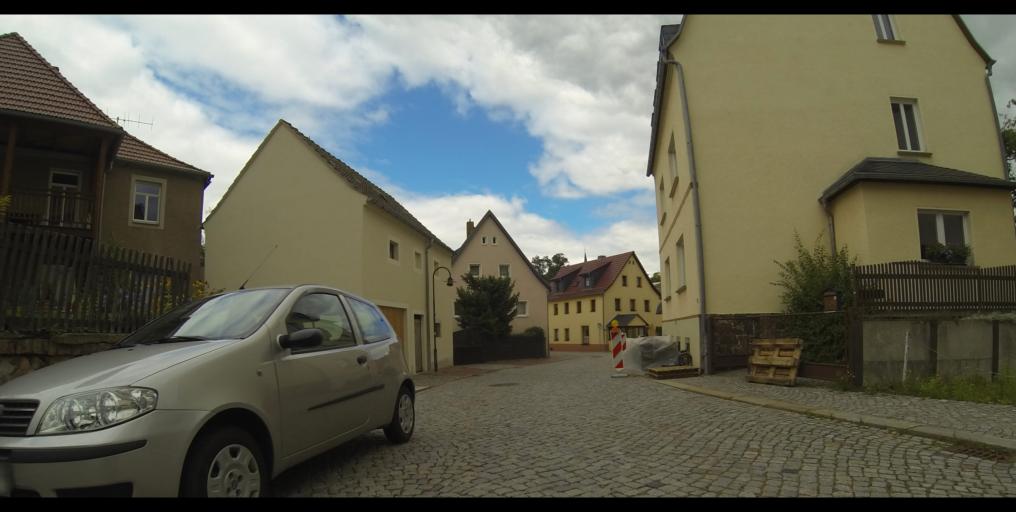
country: DE
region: Saxony
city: Wilsdruff
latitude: 51.0505
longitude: 13.5394
